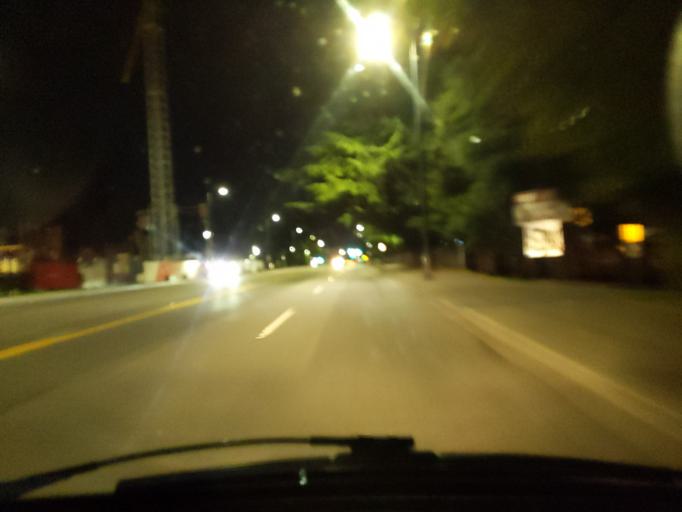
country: CA
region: British Columbia
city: New Westminster
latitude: 49.1917
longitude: -122.8526
